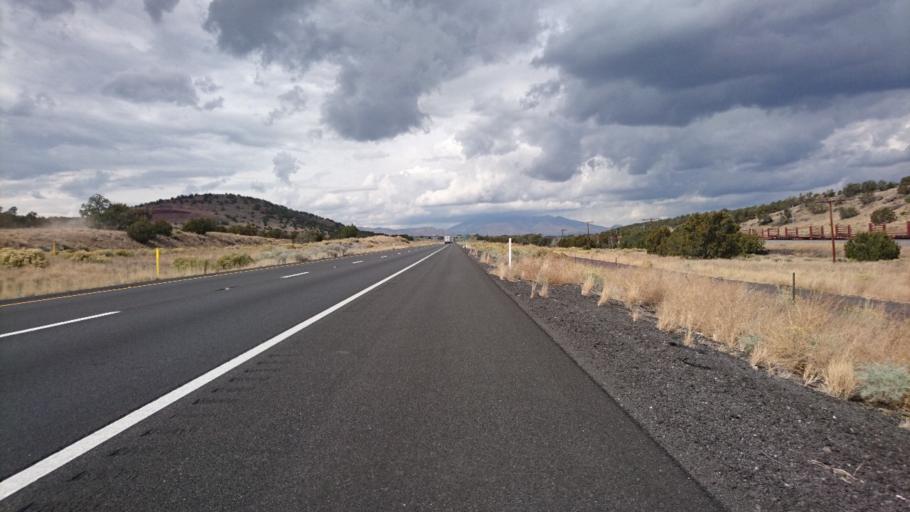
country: US
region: Arizona
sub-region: Coconino County
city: Flagstaff
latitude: 35.1972
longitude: -111.3953
